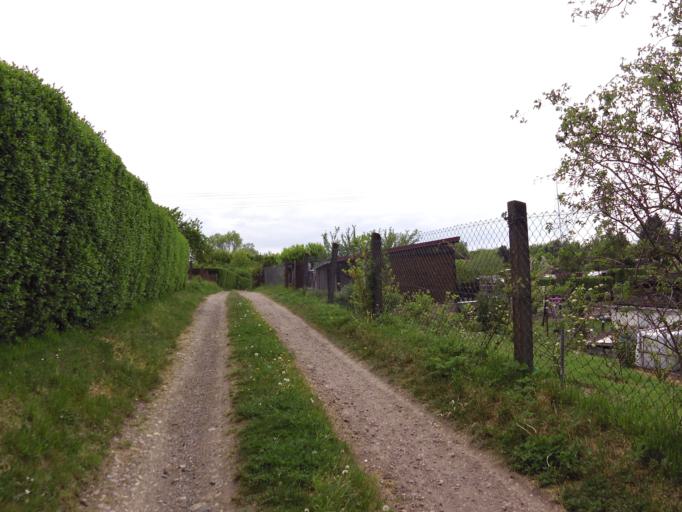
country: DE
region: Thuringia
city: Gotha
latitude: 50.9298
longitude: 10.7030
